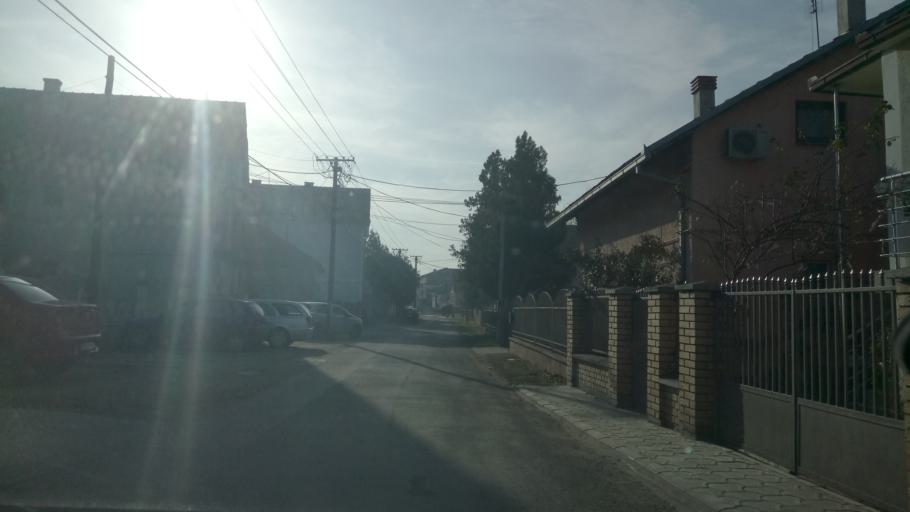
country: RS
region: Autonomna Pokrajina Vojvodina
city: Nova Pazova
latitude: 44.9520
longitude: 20.2253
